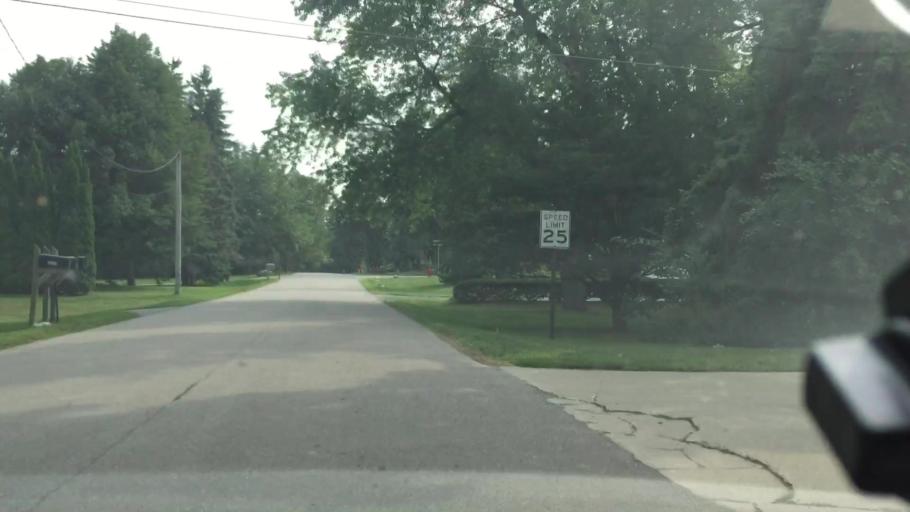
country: US
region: Michigan
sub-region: Oakland County
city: Pontiac
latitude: 42.6023
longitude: -83.2928
